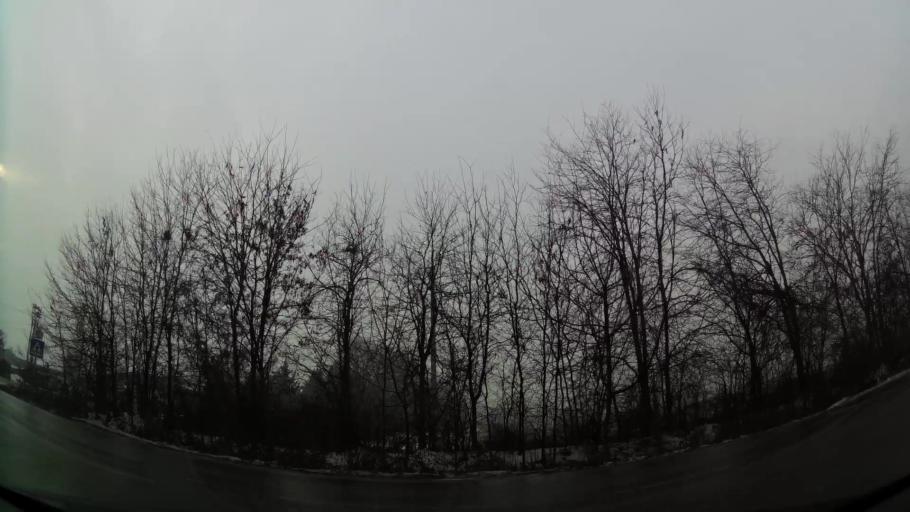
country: MK
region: Ilinden
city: Idrizovo
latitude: 41.9535
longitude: 21.5793
